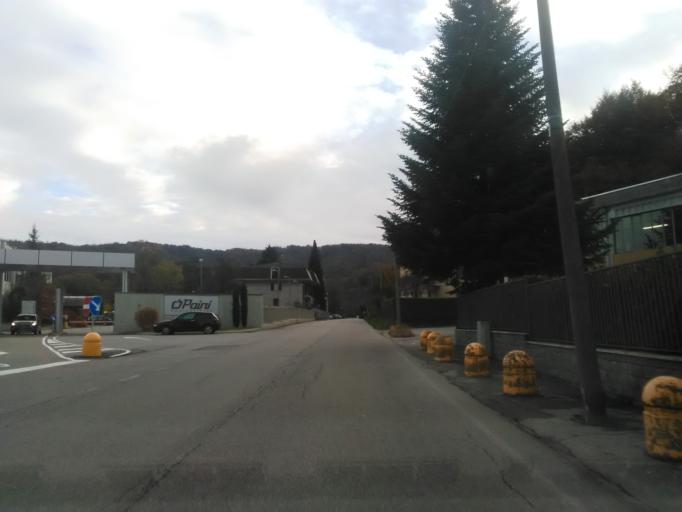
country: IT
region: Piedmont
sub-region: Provincia di Novara
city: Pogno
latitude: 45.7522
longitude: 8.3809
